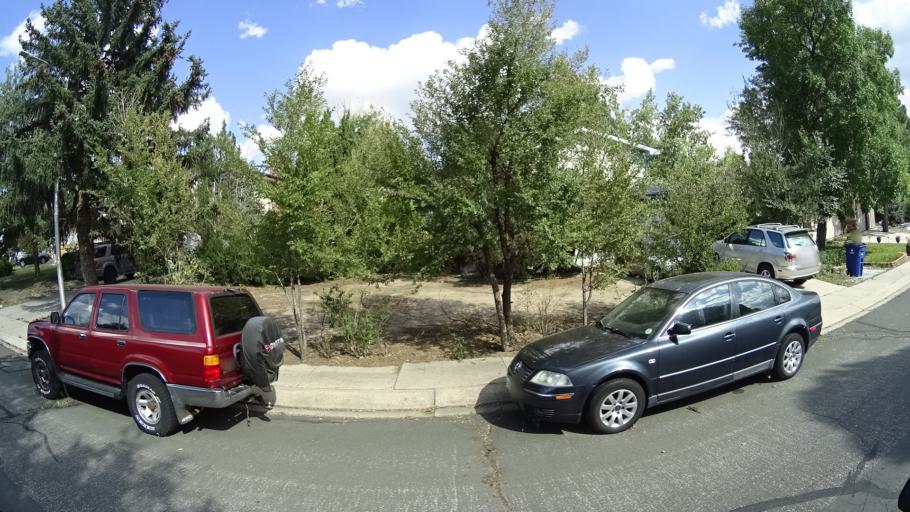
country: US
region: Colorado
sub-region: El Paso County
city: Cimarron Hills
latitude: 38.8711
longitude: -104.7304
